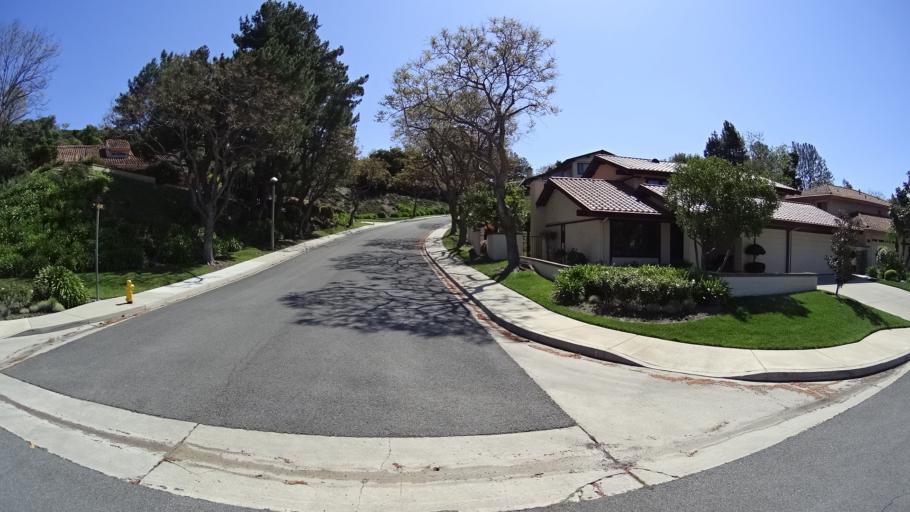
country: US
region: California
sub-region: Ventura County
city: Moorpark
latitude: 34.2335
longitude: -118.8507
